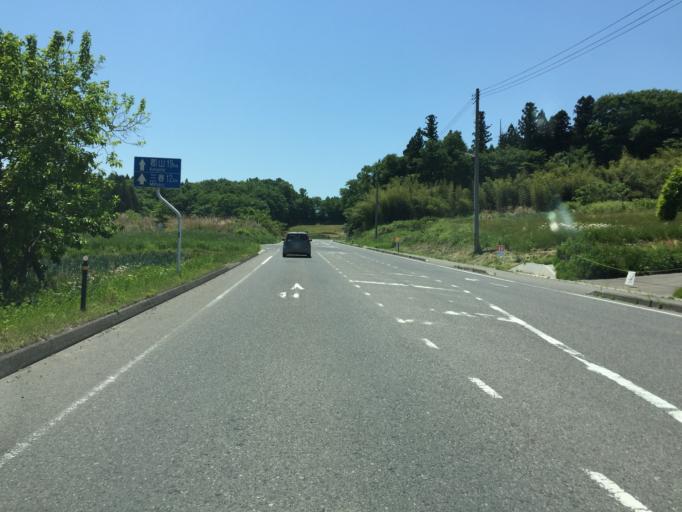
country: JP
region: Fukushima
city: Motomiya
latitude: 37.5191
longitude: 140.4584
